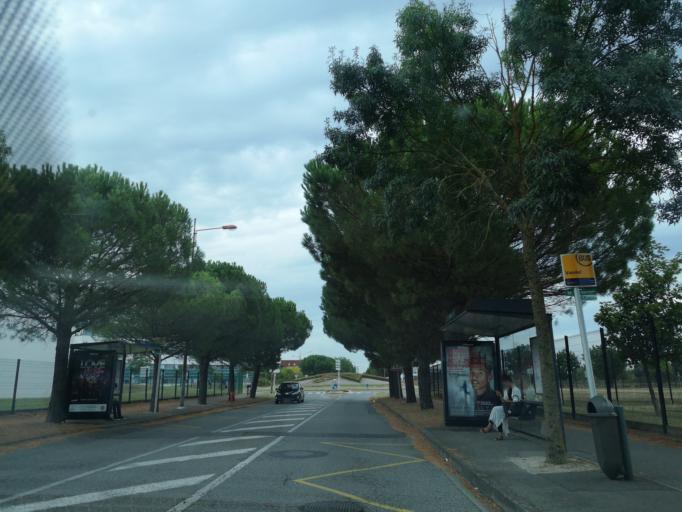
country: FR
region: Midi-Pyrenees
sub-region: Departement de la Haute-Garonne
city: Cugnaux
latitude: 43.5790
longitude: 1.3783
